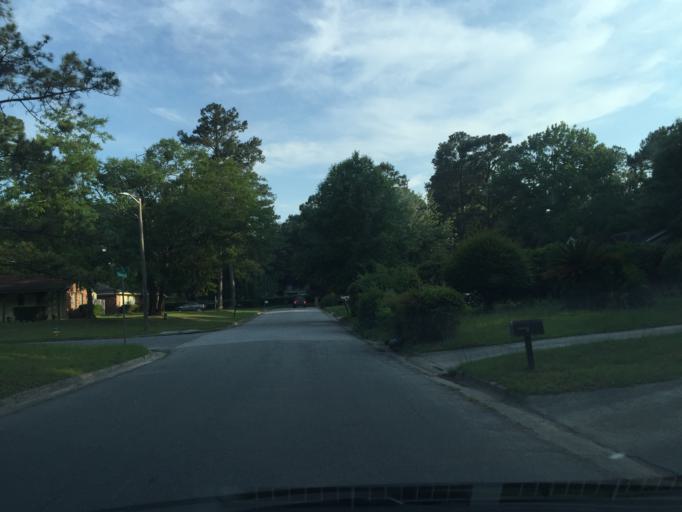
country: US
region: Georgia
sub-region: Chatham County
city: Montgomery
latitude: 31.9900
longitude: -81.1214
